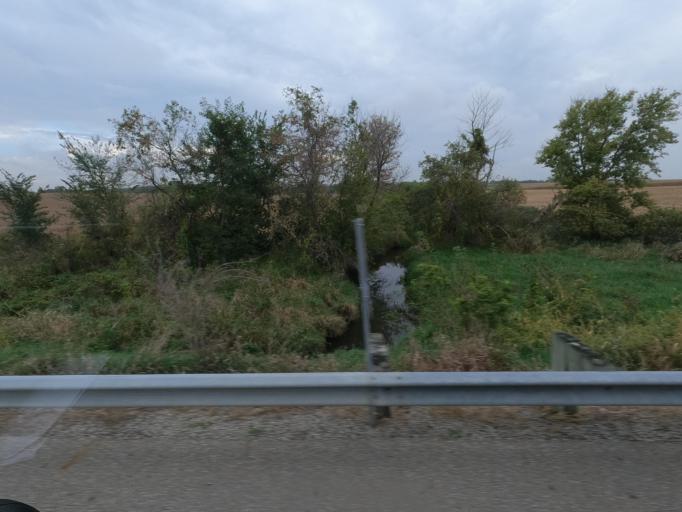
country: US
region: Iowa
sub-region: Van Buren County
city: Keosauqua
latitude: 40.8133
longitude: -91.7935
